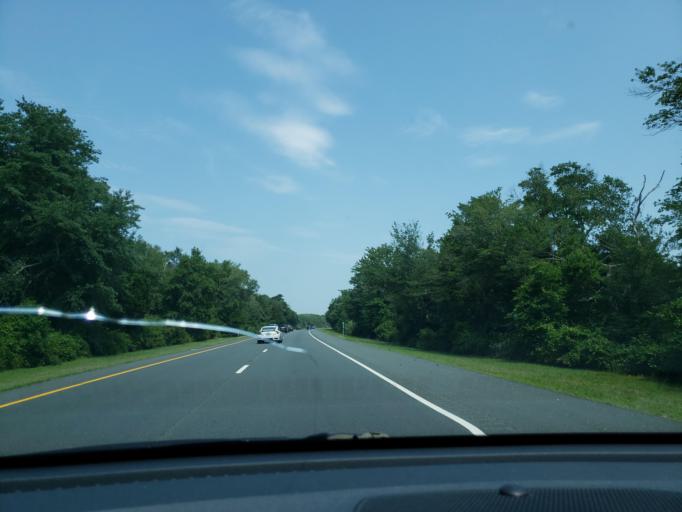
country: US
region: New Jersey
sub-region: Cape May County
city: Sea Isle City
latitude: 39.2106
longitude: -74.6929
